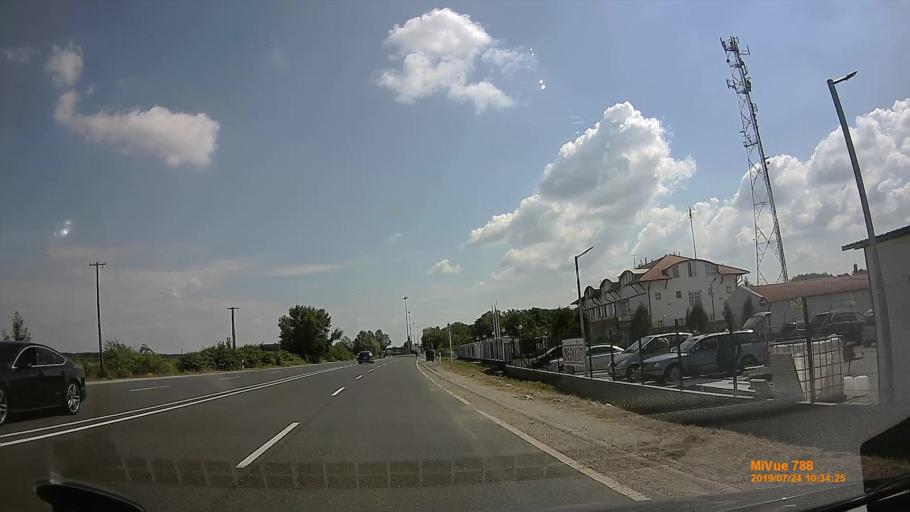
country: HU
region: Szabolcs-Szatmar-Bereg
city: Tarpa
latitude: 48.1622
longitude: 22.5642
